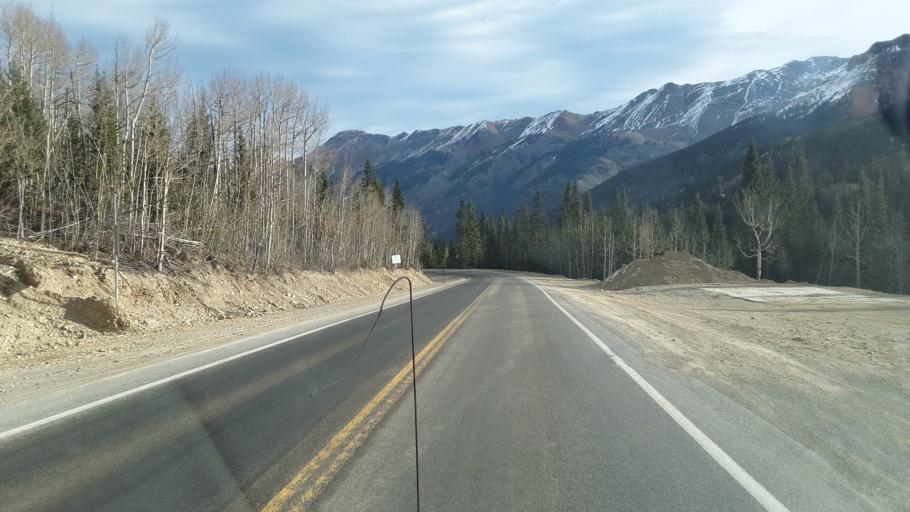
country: US
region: Colorado
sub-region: Ouray County
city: Ouray
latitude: 37.9229
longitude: -107.6968
